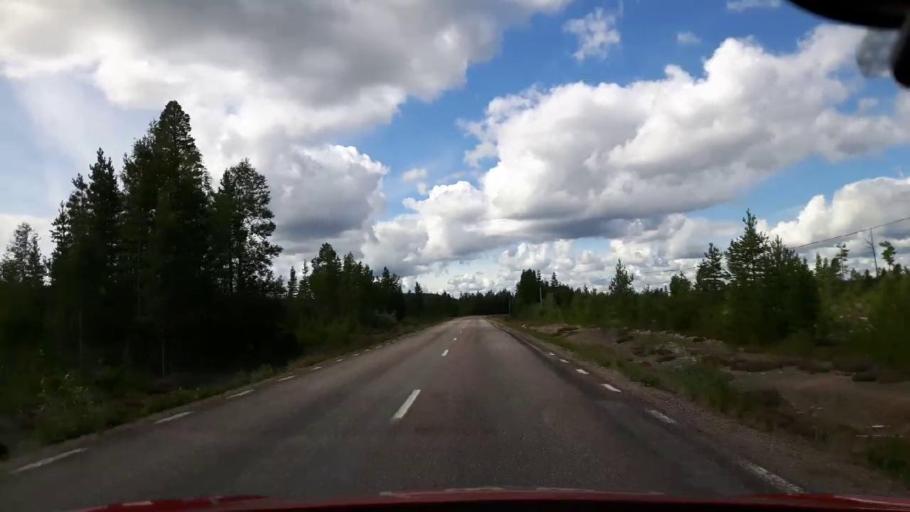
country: SE
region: Jaemtland
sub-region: Harjedalens Kommun
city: Sveg
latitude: 61.8416
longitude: 14.0316
